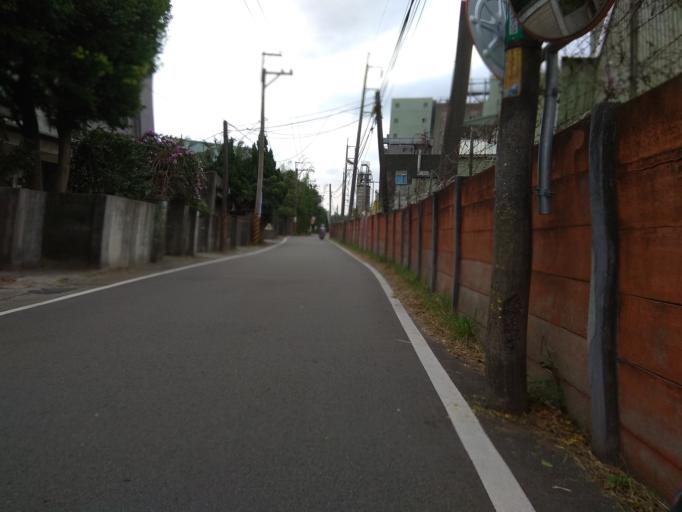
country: TW
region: Taiwan
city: Daxi
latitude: 24.9367
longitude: 121.2051
